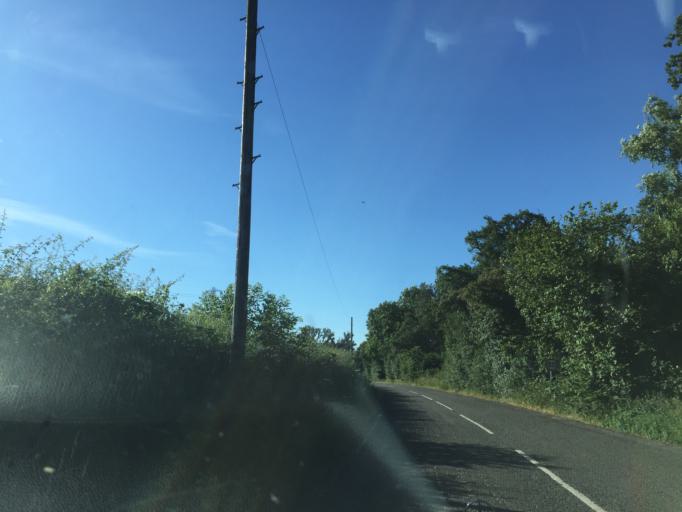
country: GB
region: England
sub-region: Warwickshire
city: Kenilworth
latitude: 52.3315
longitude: -1.6157
